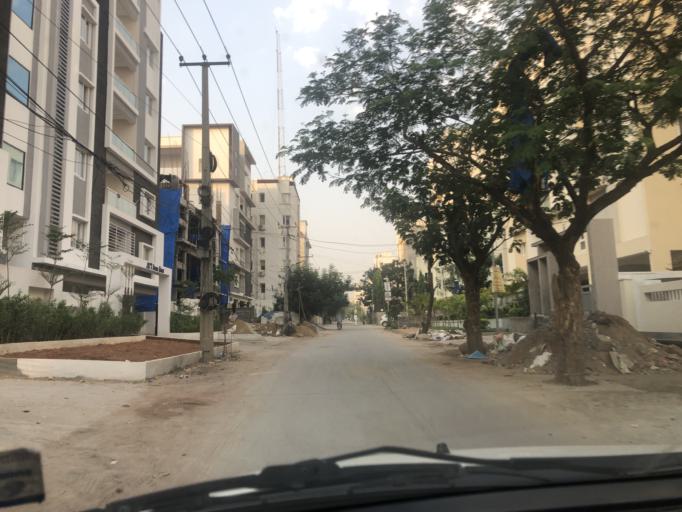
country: IN
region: Telangana
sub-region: Rangareddi
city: Kukatpalli
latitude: 17.4464
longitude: 78.3994
